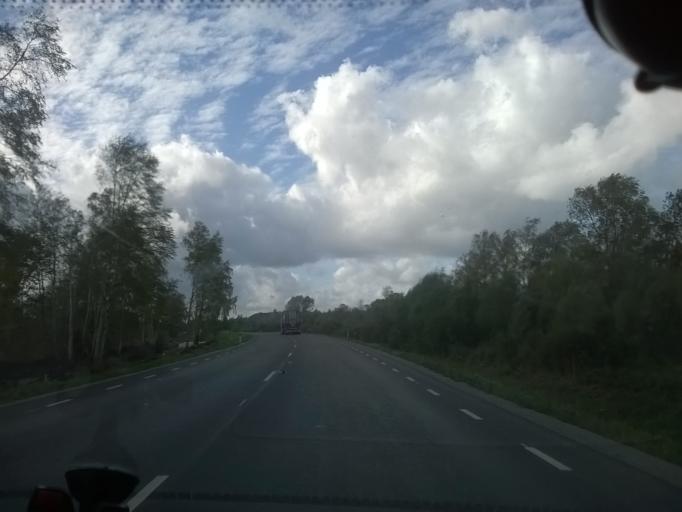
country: EE
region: Harju
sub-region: Tallinna linn
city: Kose
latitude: 59.4157
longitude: 24.8977
